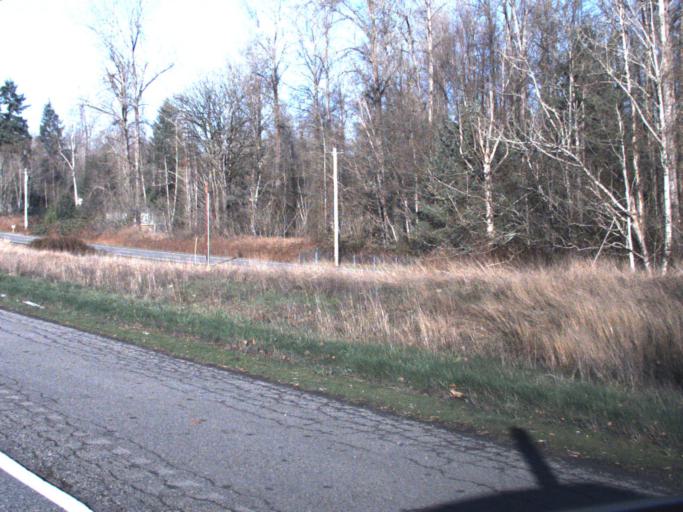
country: US
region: Washington
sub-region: Snohomish County
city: Bryant
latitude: 48.2295
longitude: -122.2304
